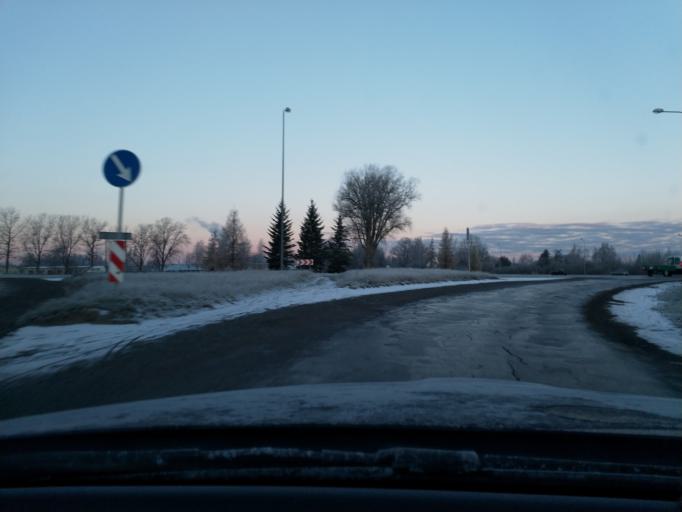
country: LV
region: Kuldigas Rajons
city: Kuldiga
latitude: 56.9566
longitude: 21.9891
